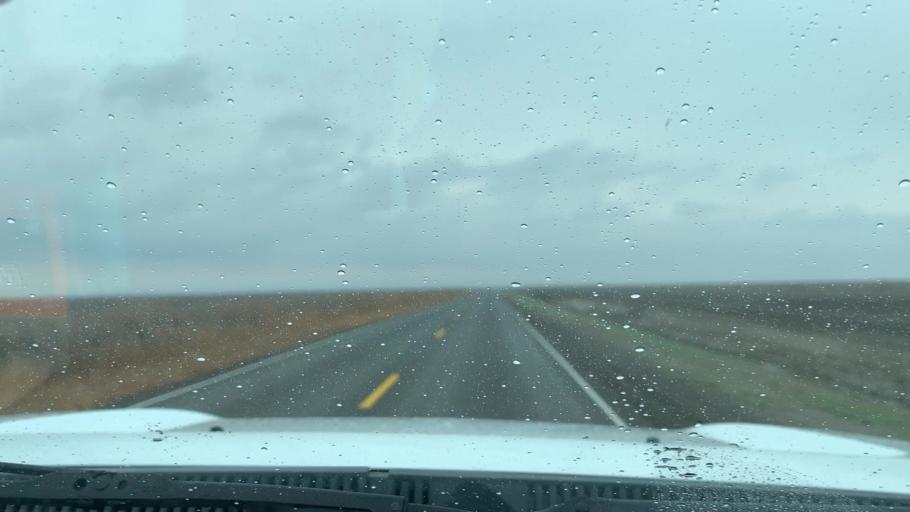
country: US
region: California
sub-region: Kings County
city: Kettleman City
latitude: 35.9340
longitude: -119.7436
